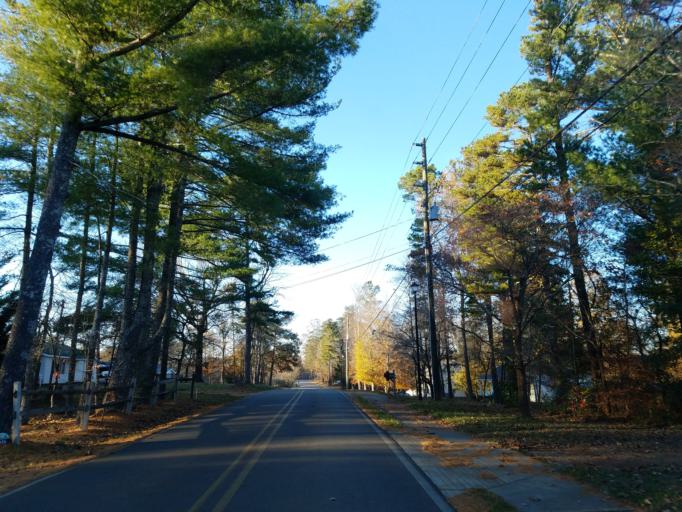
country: US
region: Georgia
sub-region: Pickens County
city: Nelson
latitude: 34.3864
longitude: -84.3688
